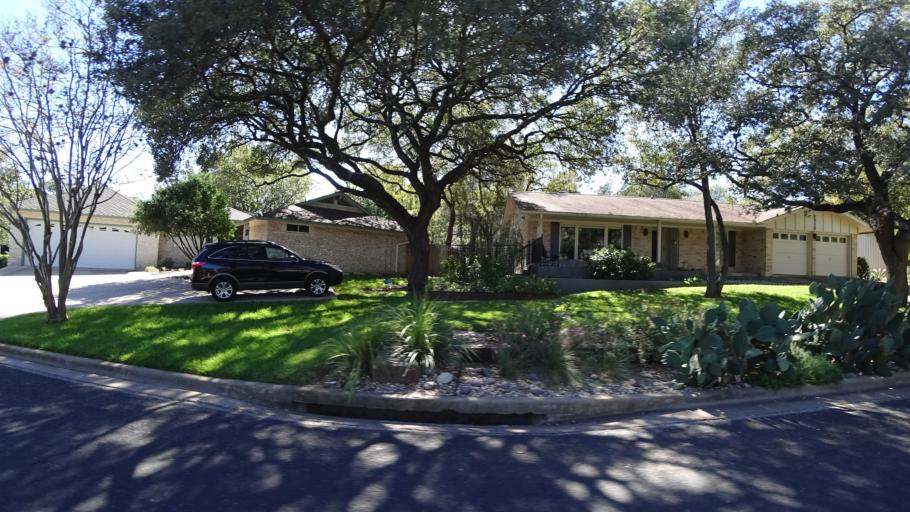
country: US
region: Texas
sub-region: Travis County
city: West Lake Hills
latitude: 30.3607
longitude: -97.7592
